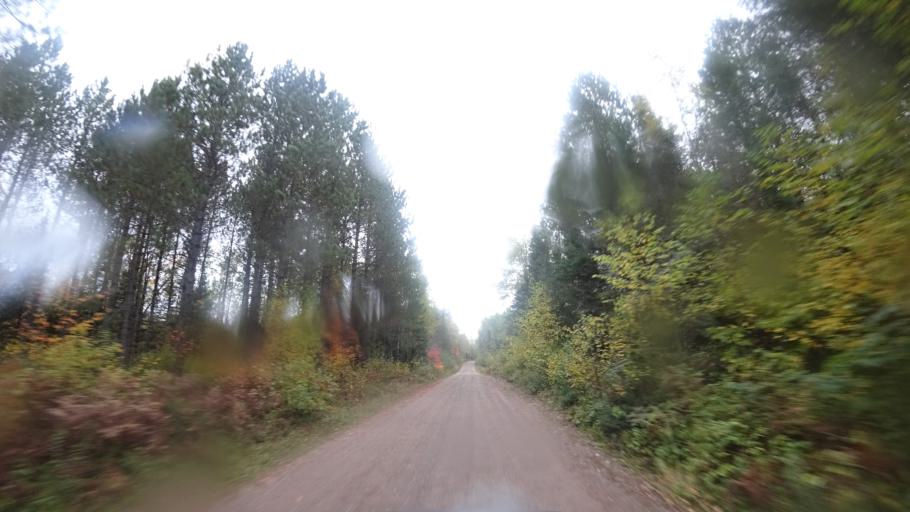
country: US
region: Wisconsin
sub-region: Sawyer County
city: Little Round Lake
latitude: 46.0892
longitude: -90.9742
